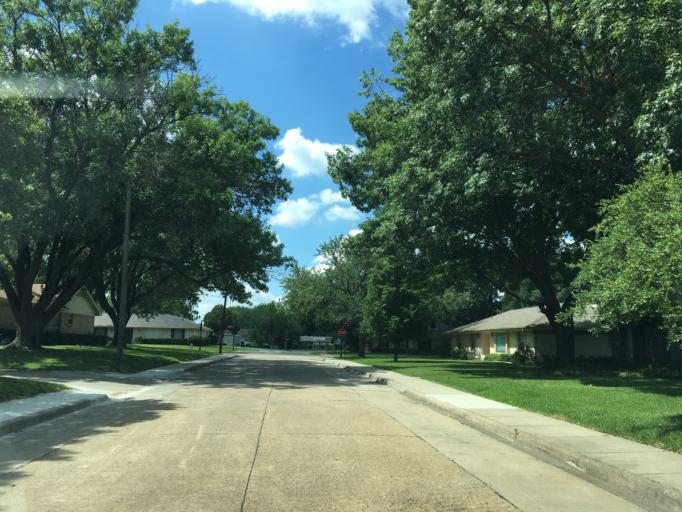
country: US
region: Texas
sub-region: Dallas County
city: Farmers Branch
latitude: 32.9216
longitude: -96.8600
